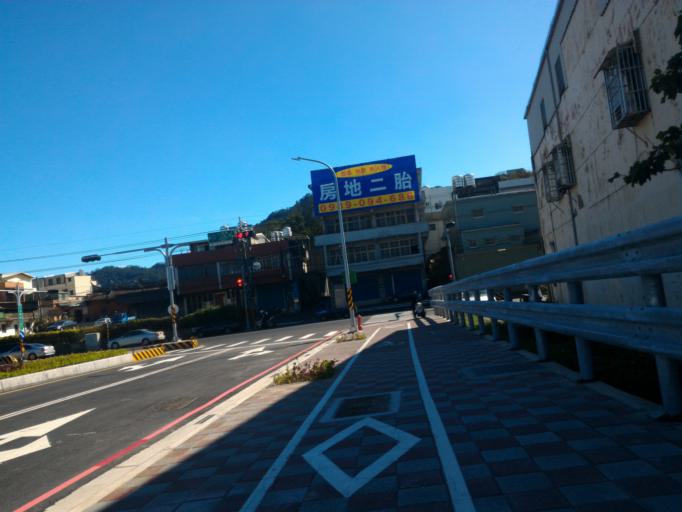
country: TW
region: Taiwan
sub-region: Taoyuan
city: Taoyuan
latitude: 24.9354
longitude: 121.3900
